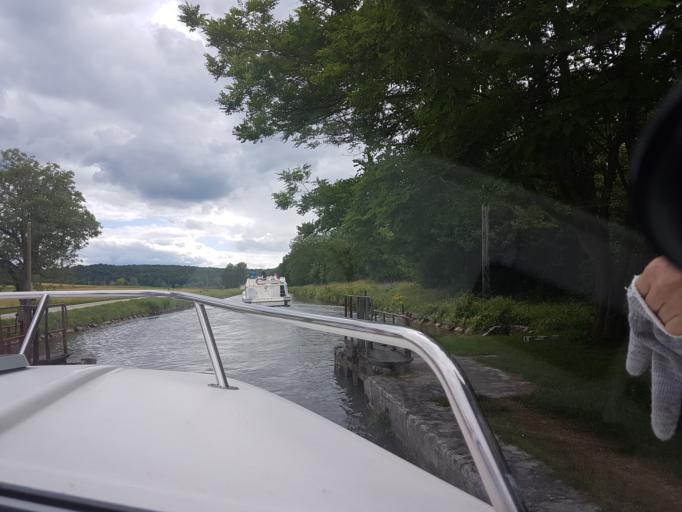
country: FR
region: Bourgogne
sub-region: Departement de l'Yonne
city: Vermenton
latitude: 47.5752
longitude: 3.6458
